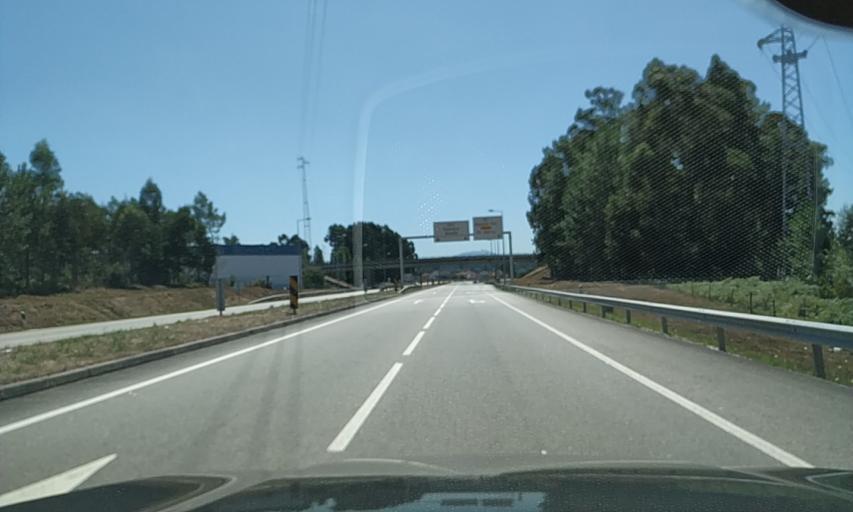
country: PT
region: Aveiro
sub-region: Agueda
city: Aguada de Cima
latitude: 40.5239
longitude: -8.4514
